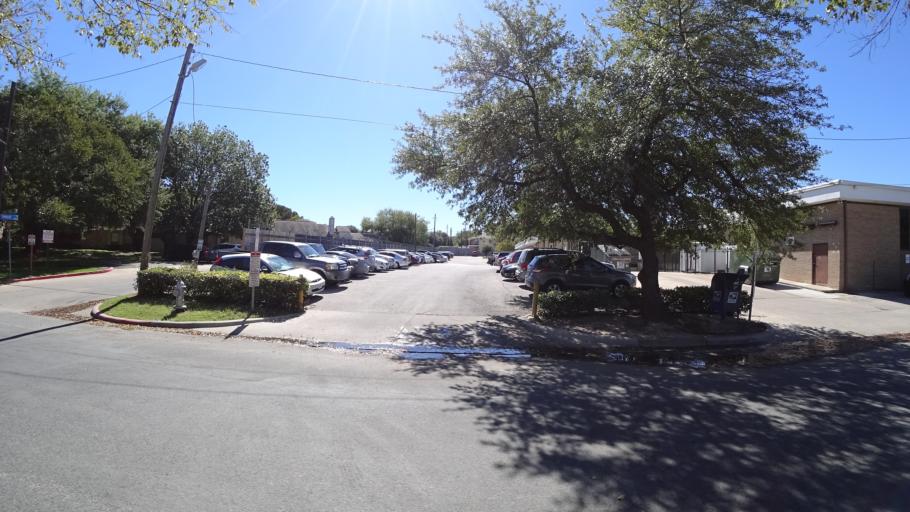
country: US
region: Texas
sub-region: Travis County
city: Austin
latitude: 30.2276
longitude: -97.7428
